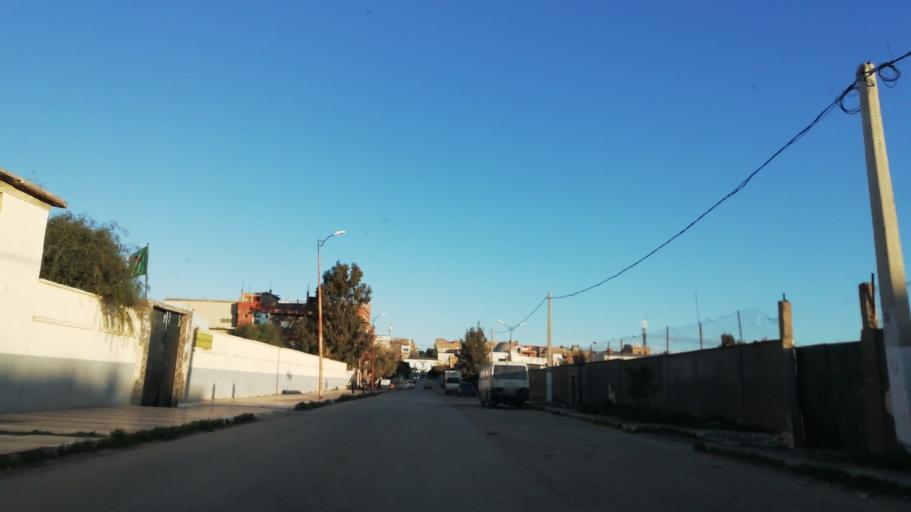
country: DZ
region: Oran
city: Sidi ech Chahmi
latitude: 35.6929
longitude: -0.5053
